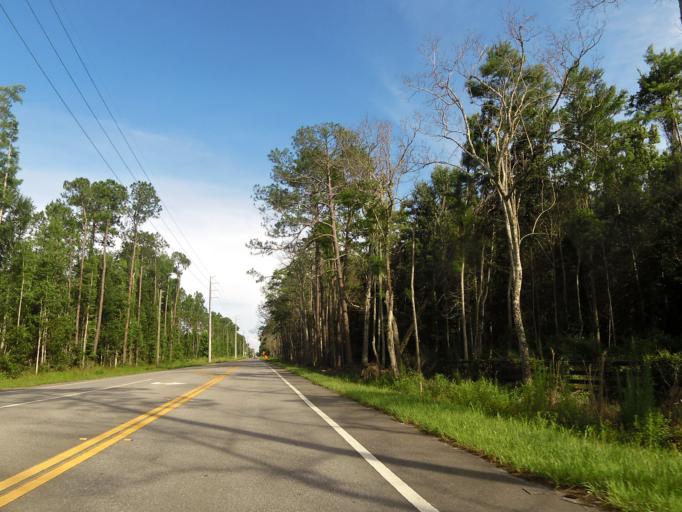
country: US
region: Florida
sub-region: Clay County
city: Green Cove Springs
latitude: 30.0024
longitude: -81.5466
